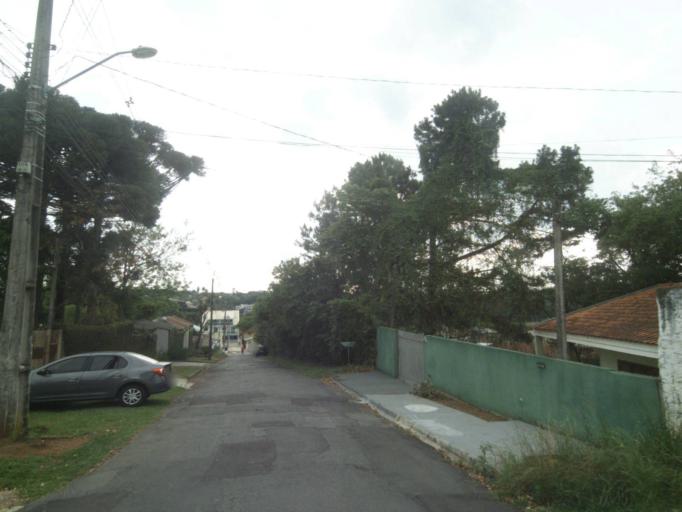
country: BR
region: Parana
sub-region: Curitiba
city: Curitiba
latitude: -25.3941
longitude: -49.3000
